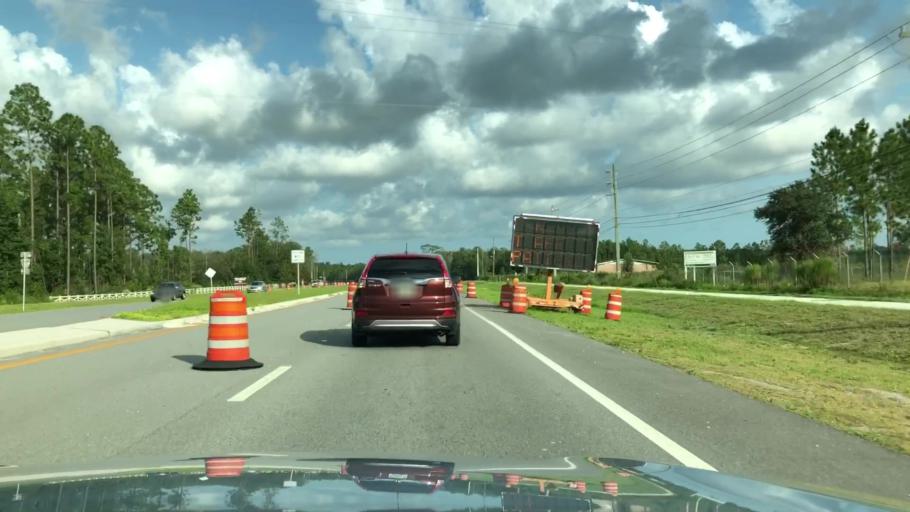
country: US
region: Florida
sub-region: Saint Johns County
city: Fruit Cove
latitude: 30.1031
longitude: -81.5386
